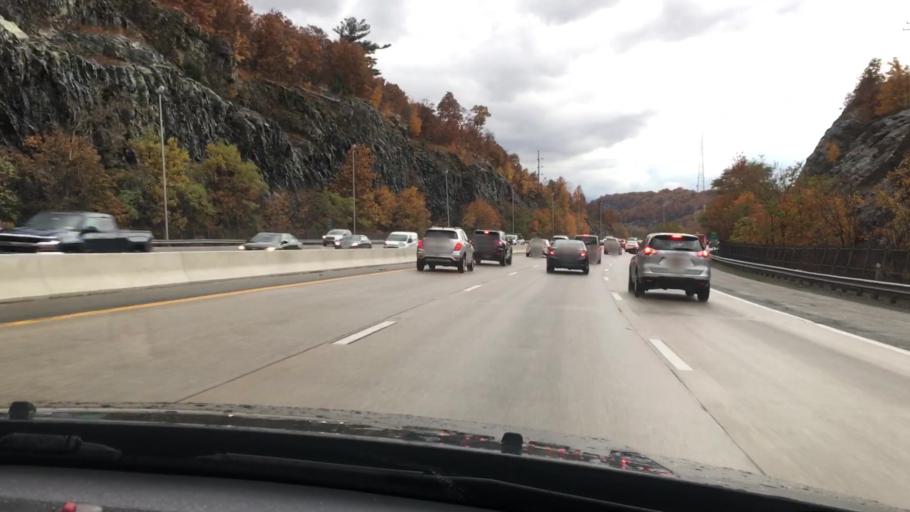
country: US
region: New Jersey
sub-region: Passaic County
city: Pompton Lakes
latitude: 41.0204
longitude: -74.2928
